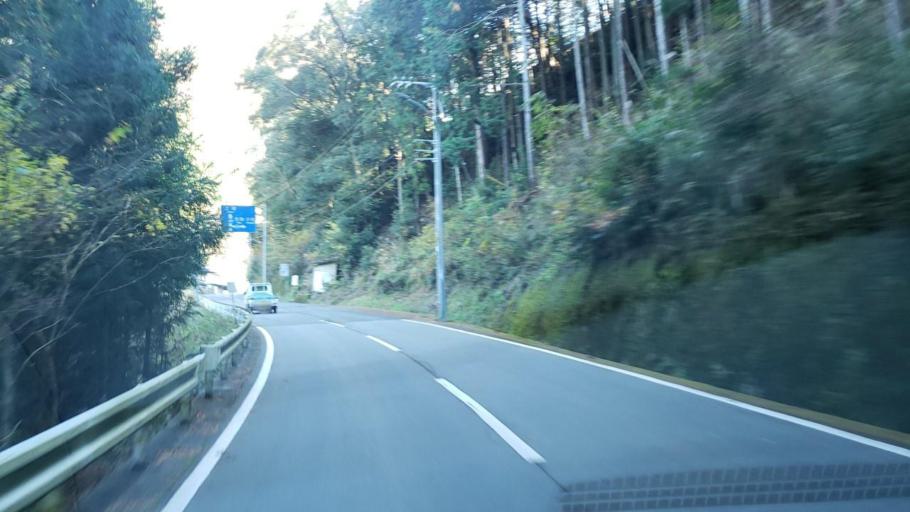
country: JP
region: Tokushima
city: Wakimachi
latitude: 34.0024
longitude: 134.0362
